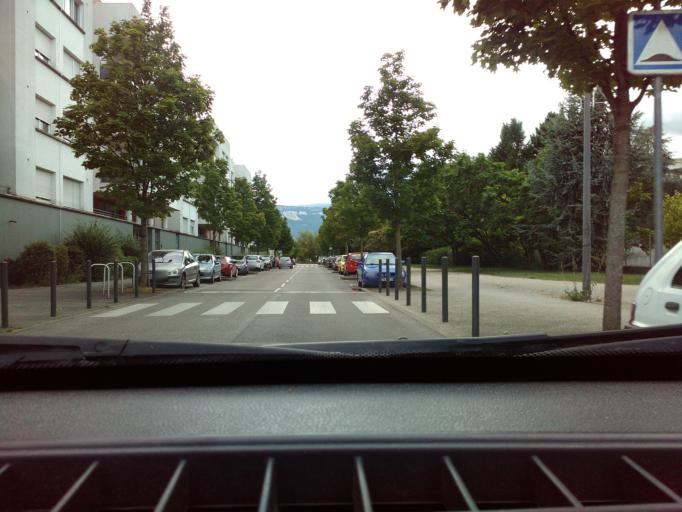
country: FR
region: Rhone-Alpes
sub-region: Departement de l'Isere
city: Saint-Martin-d'Heres
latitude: 45.1788
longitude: 5.7581
